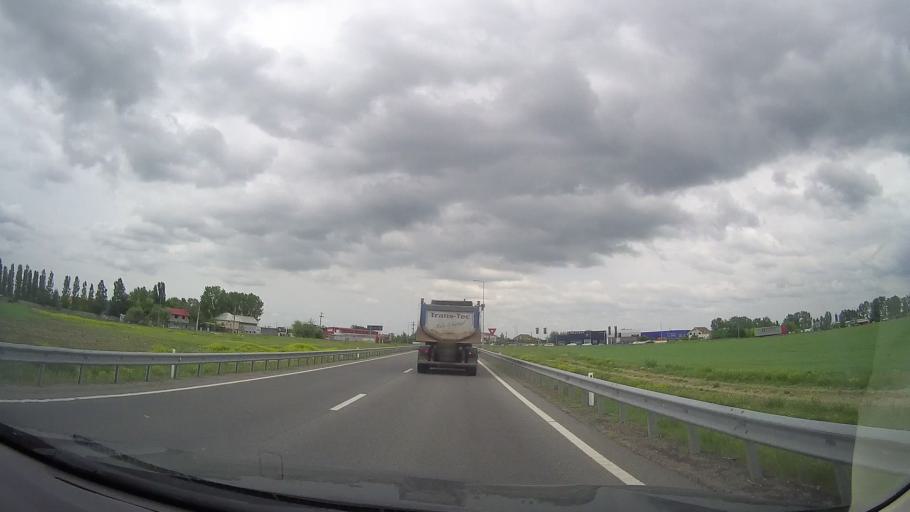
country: RO
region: Dolj
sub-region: Comuna Pielesti
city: Pielesti
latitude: 44.3123
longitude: 23.9111
